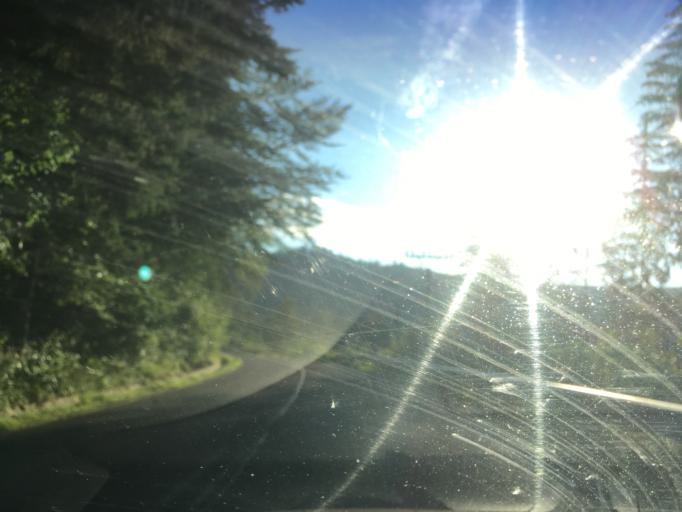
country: PL
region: Lesser Poland Voivodeship
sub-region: Powiat tatrzanski
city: Bukowina Tatrzanska
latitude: 49.2697
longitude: 20.1311
